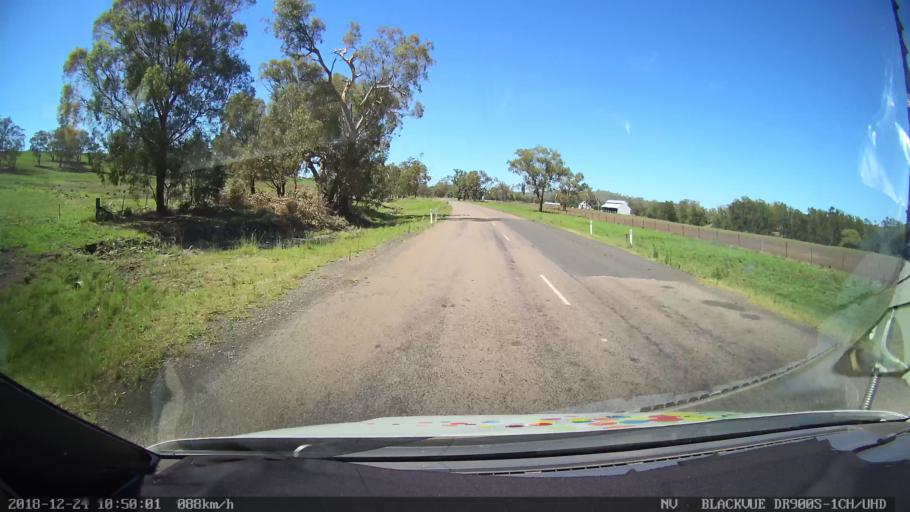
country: AU
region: New South Wales
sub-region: Upper Hunter Shire
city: Merriwa
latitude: -31.9549
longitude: 150.4249
